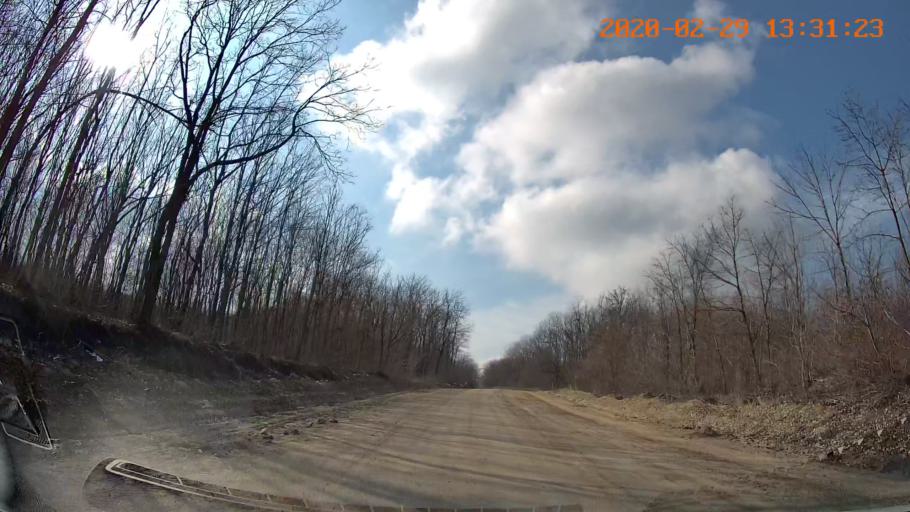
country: MD
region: Telenesti
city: Camenca
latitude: 47.8821
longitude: 28.6198
